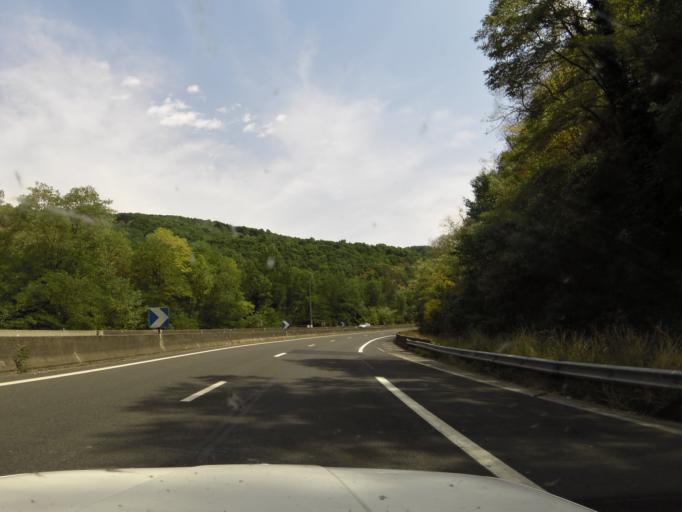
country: FR
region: Auvergne
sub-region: Departement du Puy-de-Dome
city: Issoire
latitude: 45.5894
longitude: 3.2455
